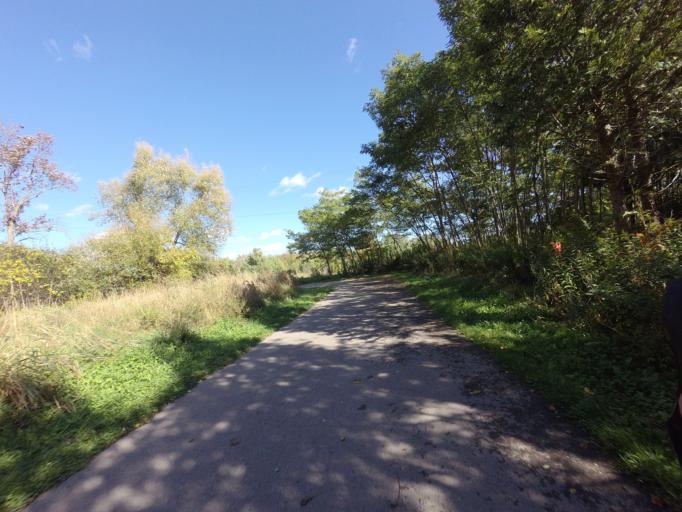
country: CA
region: Ontario
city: Ajax
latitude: 43.8524
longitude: -78.9658
